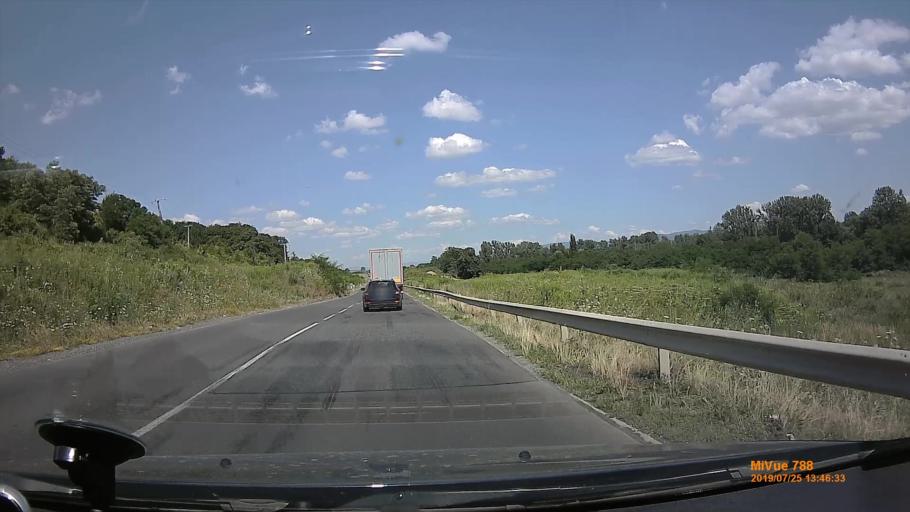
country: HU
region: Borsod-Abauj-Zemplen
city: Gonc
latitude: 48.4884
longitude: 21.2129
